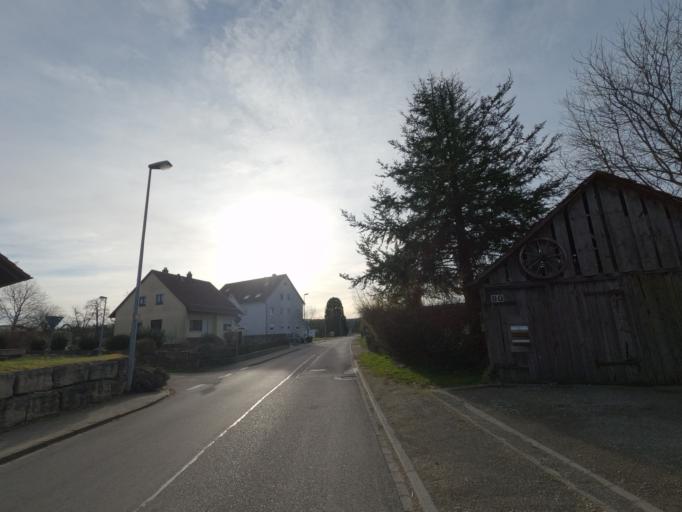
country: DE
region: Baden-Wuerttemberg
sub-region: Regierungsbezirk Stuttgart
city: Hattenhofen
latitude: 48.6819
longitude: 9.5847
